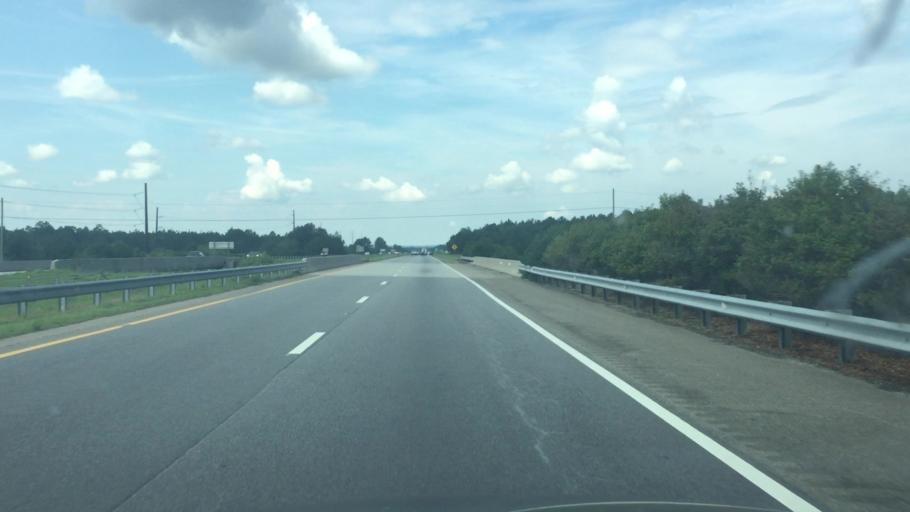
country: US
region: North Carolina
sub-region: Richmond County
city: Hamlet
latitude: 34.8561
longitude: -79.6947
